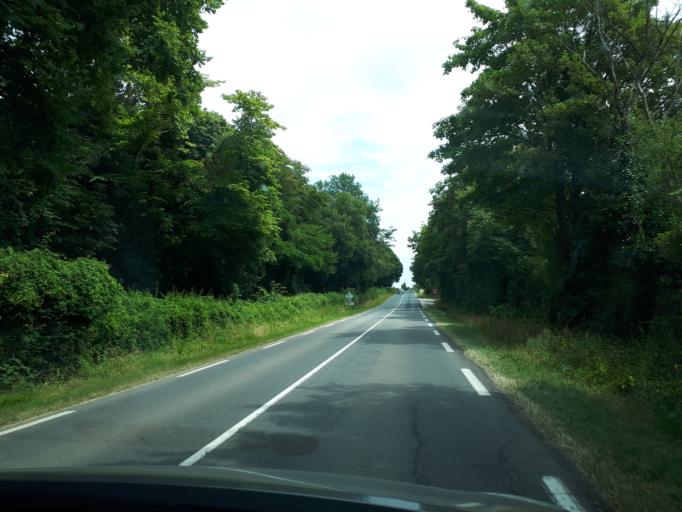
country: FR
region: Centre
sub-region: Departement du Cher
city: Rians
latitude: 47.2229
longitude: 2.6322
